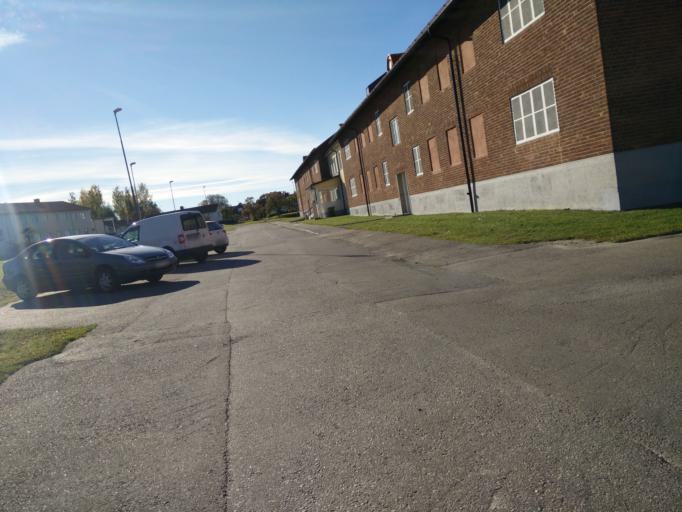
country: SE
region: Vaesternorrland
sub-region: Haernoesands Kommun
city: Haernoesand
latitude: 62.6410
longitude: 17.9623
